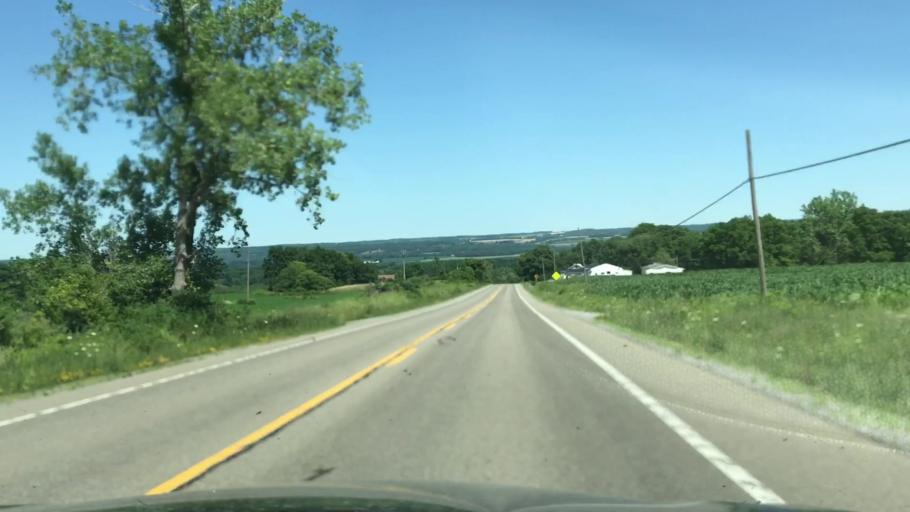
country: US
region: New York
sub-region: Livingston County
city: Mount Morris
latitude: 42.7551
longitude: -77.9092
